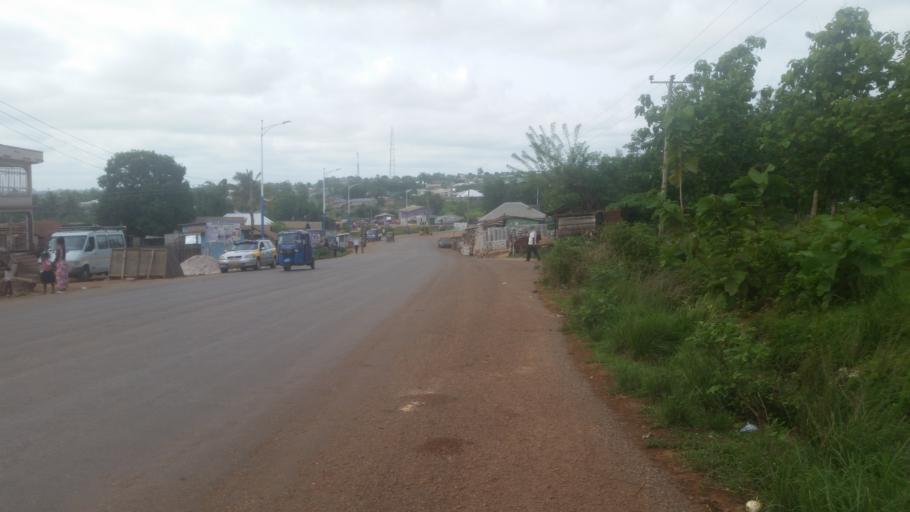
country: GH
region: Western
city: Bibiani
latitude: 6.7997
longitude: -2.5179
